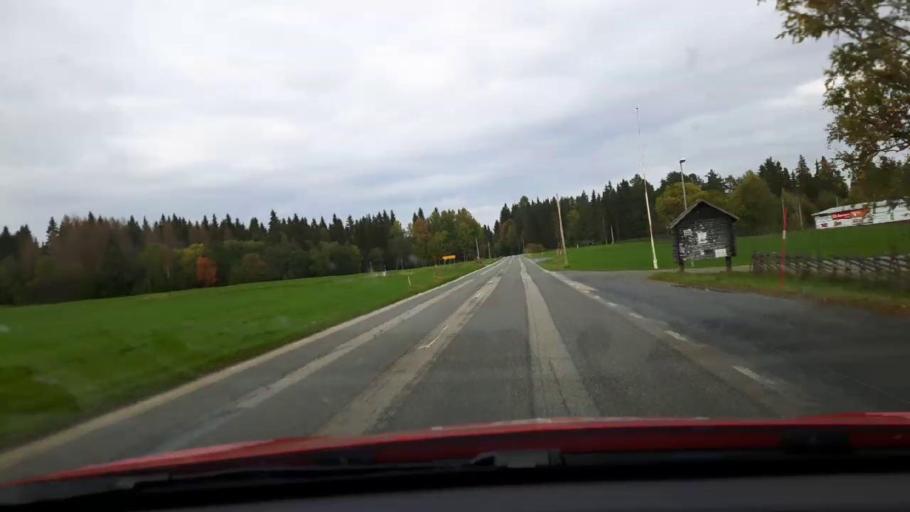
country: SE
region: Jaemtland
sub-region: Bergs Kommun
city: Hoverberg
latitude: 62.7812
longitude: 14.4330
